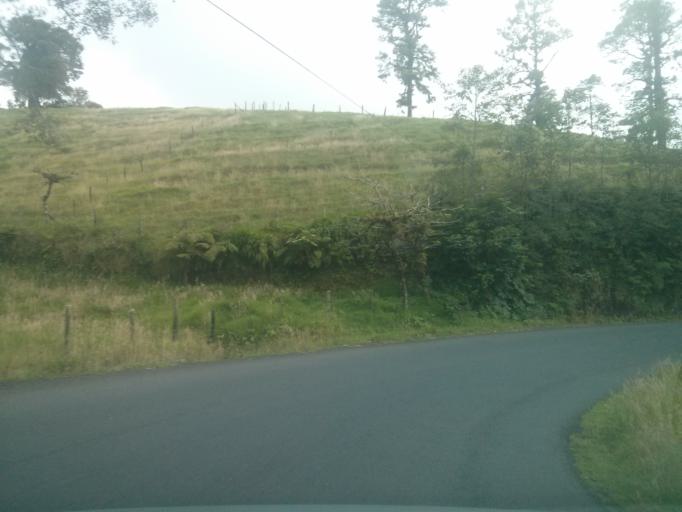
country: CR
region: Heredia
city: Santo Domingo
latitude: 10.1483
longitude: -84.1533
